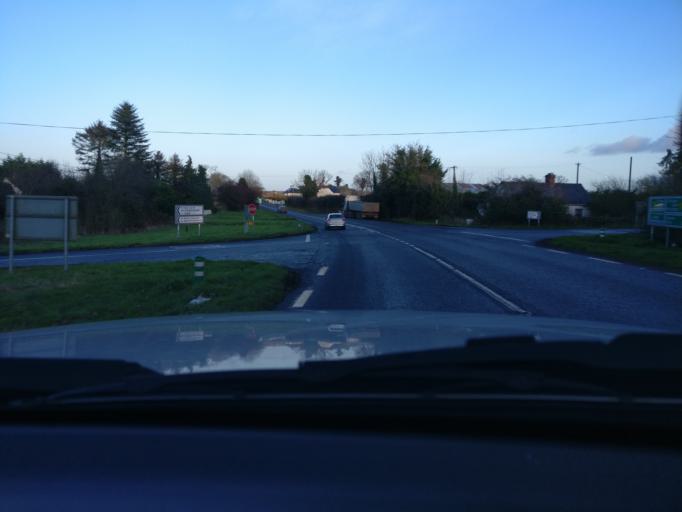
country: IE
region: Leinster
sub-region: Lu
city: Ardee
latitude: 53.8443
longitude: -6.6039
